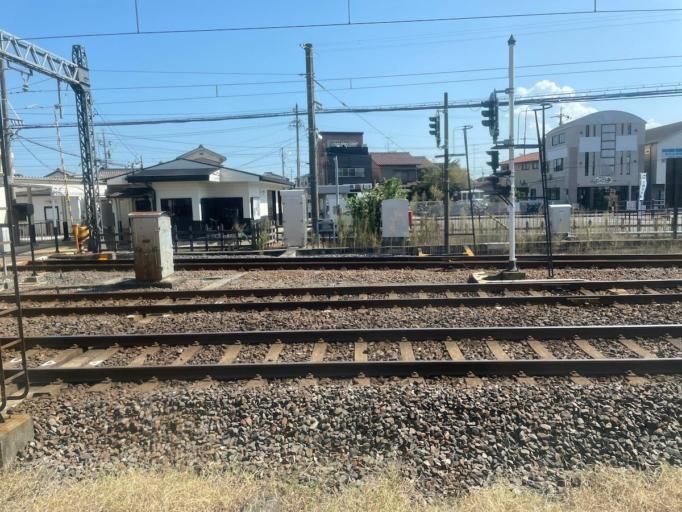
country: JP
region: Mie
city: Tsu-shi
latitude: 34.7435
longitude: 136.5138
